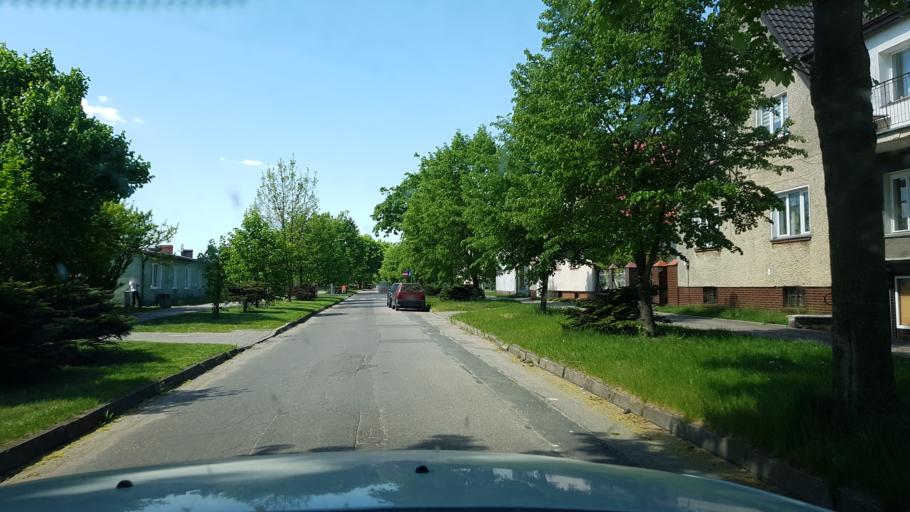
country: PL
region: West Pomeranian Voivodeship
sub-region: Powiat bialogardzki
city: Bialogard
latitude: 54.0045
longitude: 16.0064
